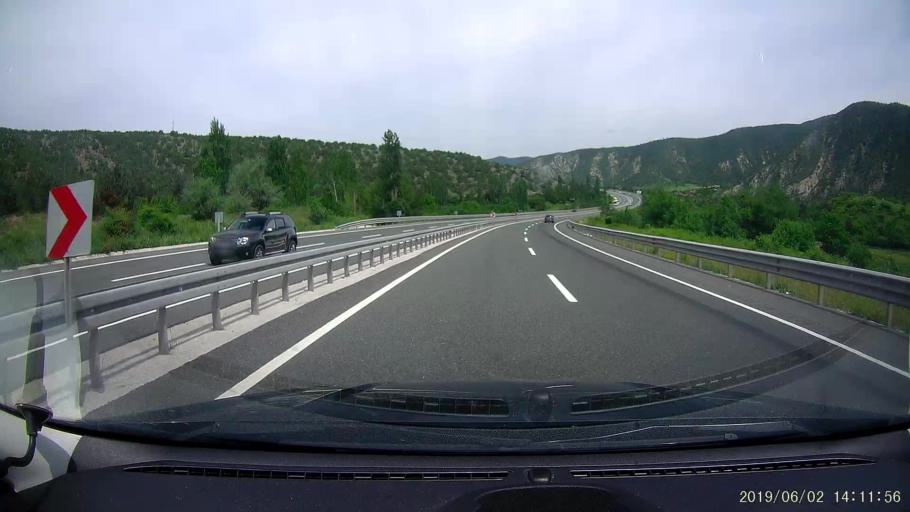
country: TR
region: Cankiri
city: Yaprakli
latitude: 40.9118
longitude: 33.7972
